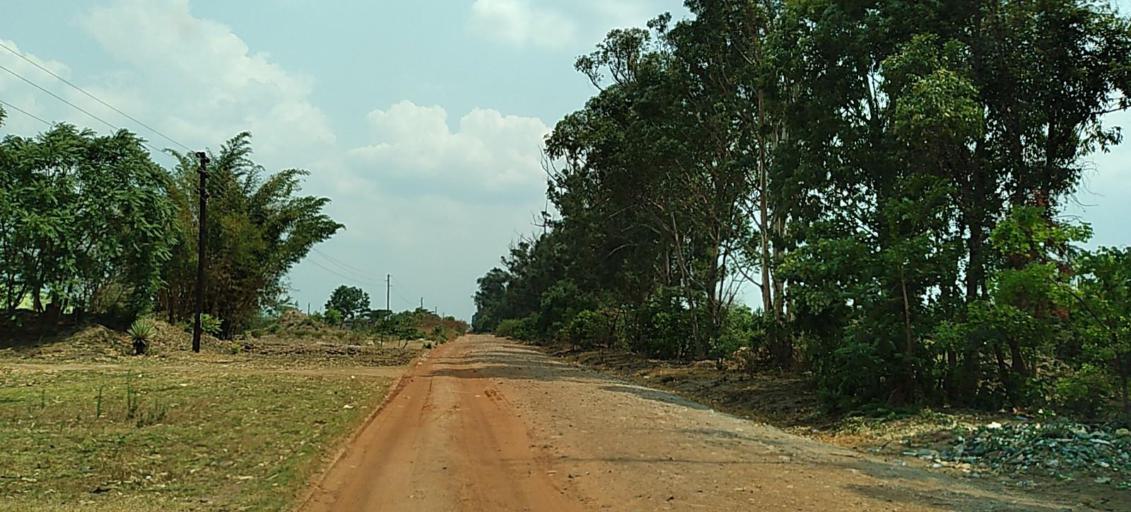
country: ZM
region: Copperbelt
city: Kalulushi
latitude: -12.8291
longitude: 28.0772
